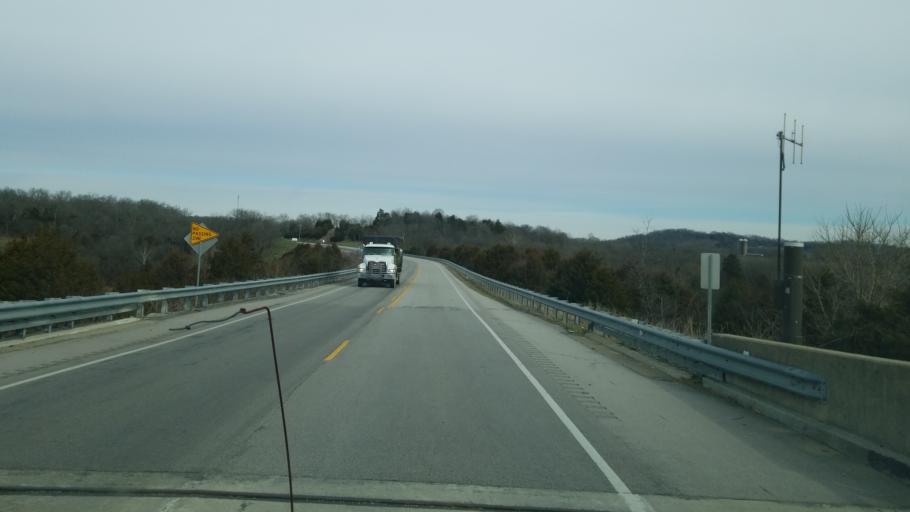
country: US
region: Kentucky
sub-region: Nicholas County
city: Carlisle
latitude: 38.4206
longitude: -83.9969
